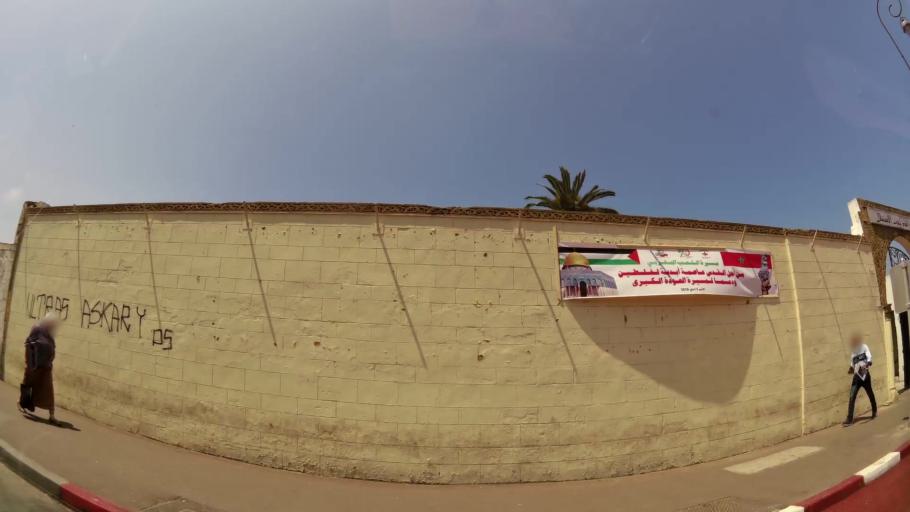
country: MA
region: Rabat-Sale-Zemmour-Zaer
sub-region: Rabat
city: Rabat
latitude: 34.0206
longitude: -6.8404
